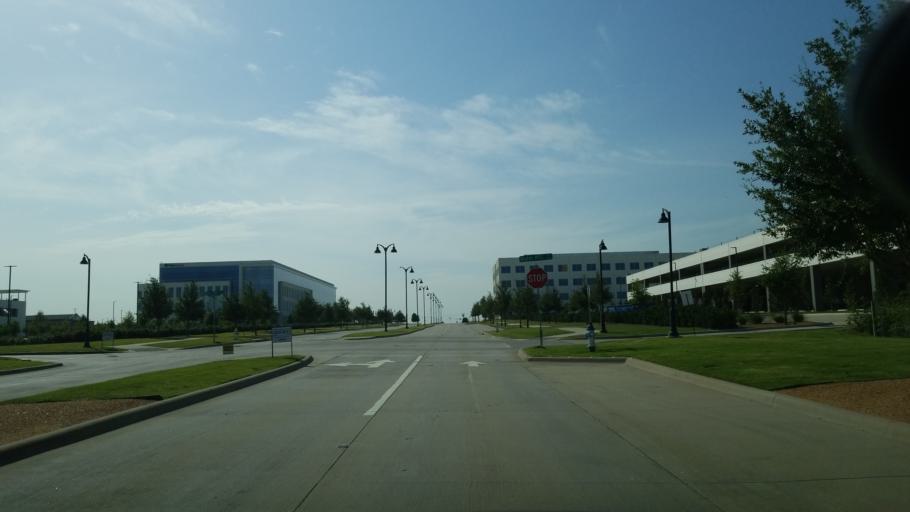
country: US
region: Texas
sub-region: Dallas County
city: Coppell
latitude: 32.9318
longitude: -96.9903
